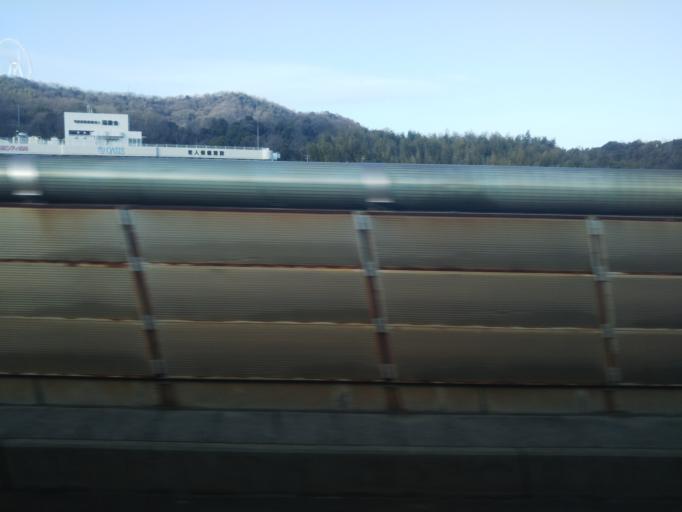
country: JP
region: Kagawa
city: Sakaidecho
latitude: 34.4517
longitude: 133.8074
